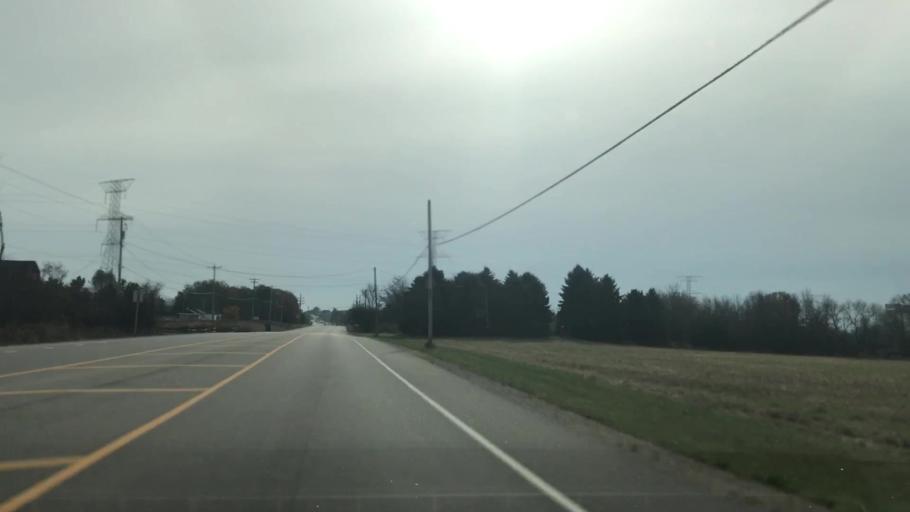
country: US
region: Wisconsin
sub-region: Waukesha County
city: Menomonee Falls
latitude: 43.2018
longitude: -88.1509
